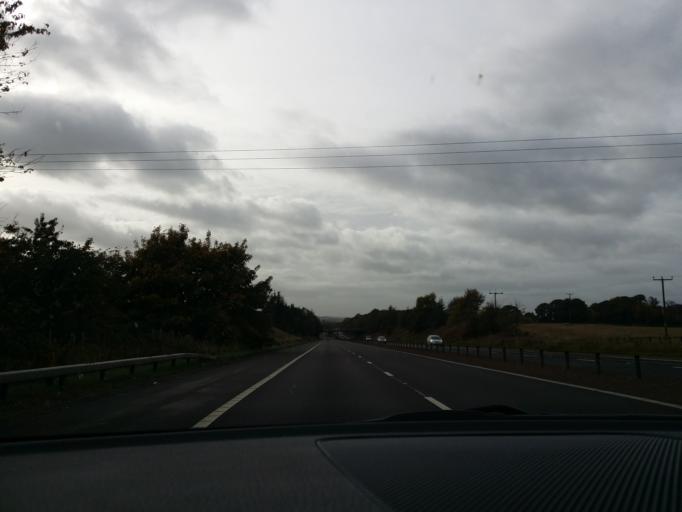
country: GB
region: Scotland
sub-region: West Lothian
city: Linlithgow
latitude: 55.9873
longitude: -3.5832
